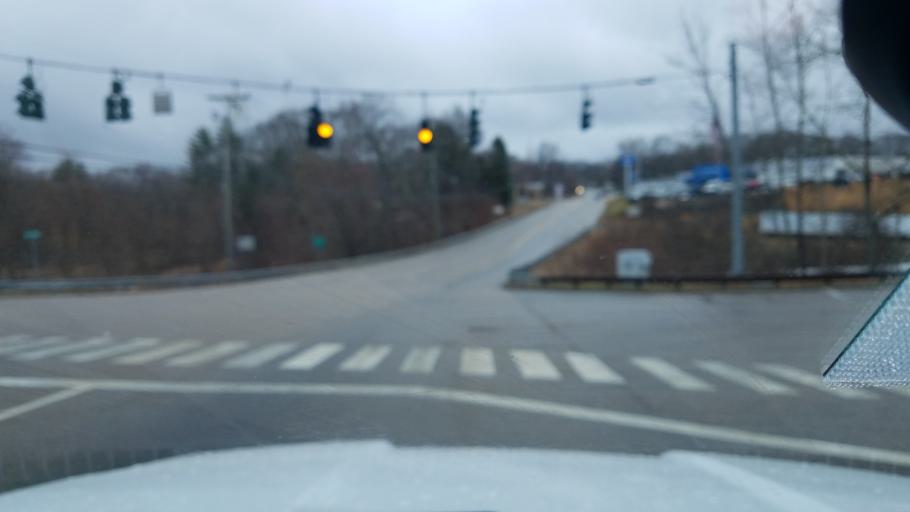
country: US
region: Connecticut
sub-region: New London County
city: Norwich
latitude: 41.4943
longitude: -72.1010
